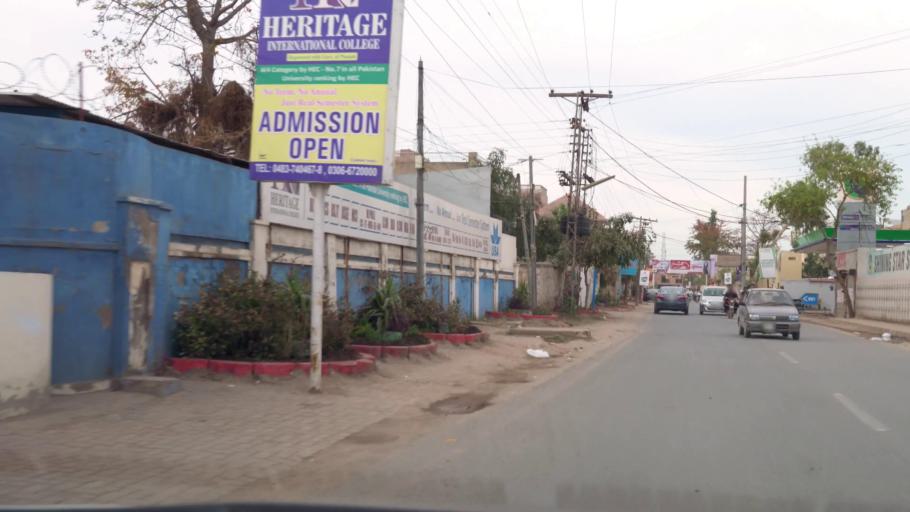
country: PK
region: Punjab
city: Sargodha
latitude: 32.0761
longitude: 72.6787
